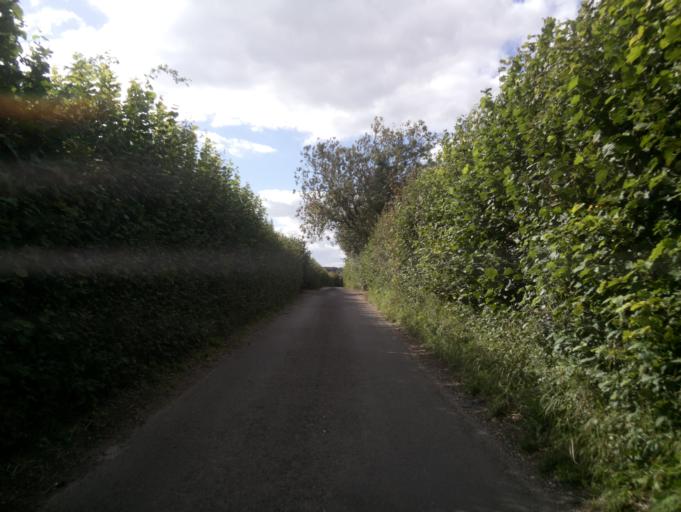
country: GB
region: England
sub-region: Hampshire
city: Chandlers Ford
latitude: 51.0541
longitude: -1.3797
